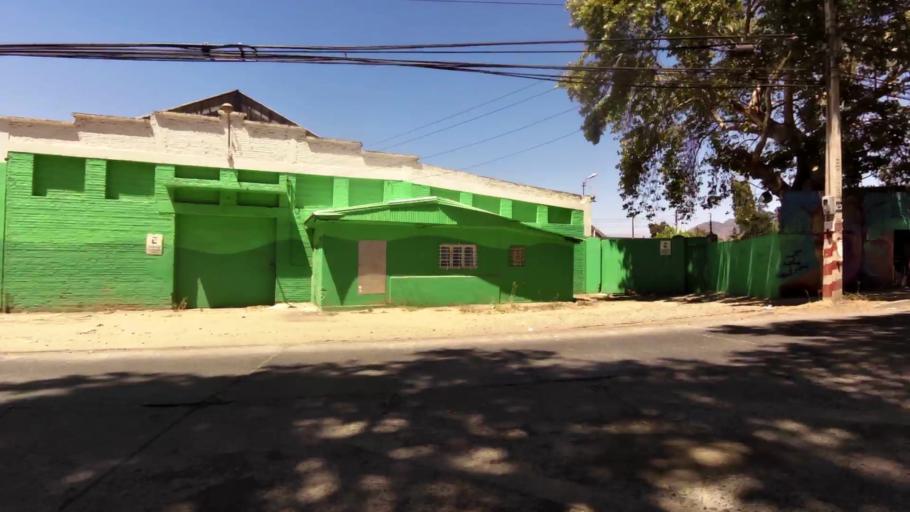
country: CL
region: O'Higgins
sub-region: Provincia de Cachapoal
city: Rancagua
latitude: -34.1662
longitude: -70.7525
